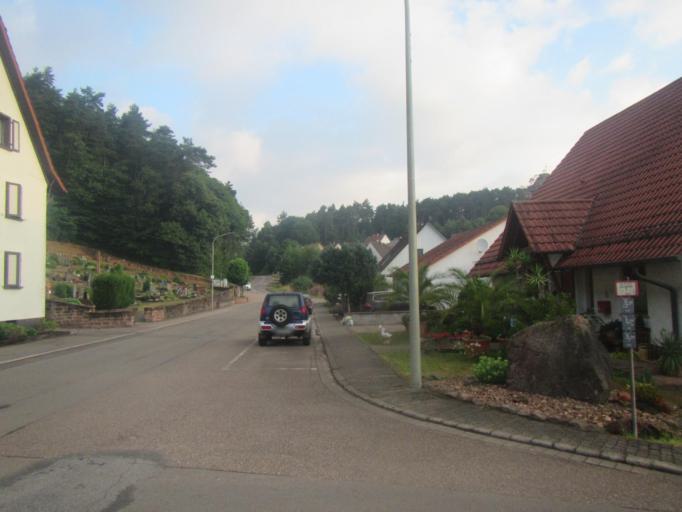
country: DE
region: Rheinland-Pfalz
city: Gossersweiler-Stein
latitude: 49.1557
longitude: 7.9346
